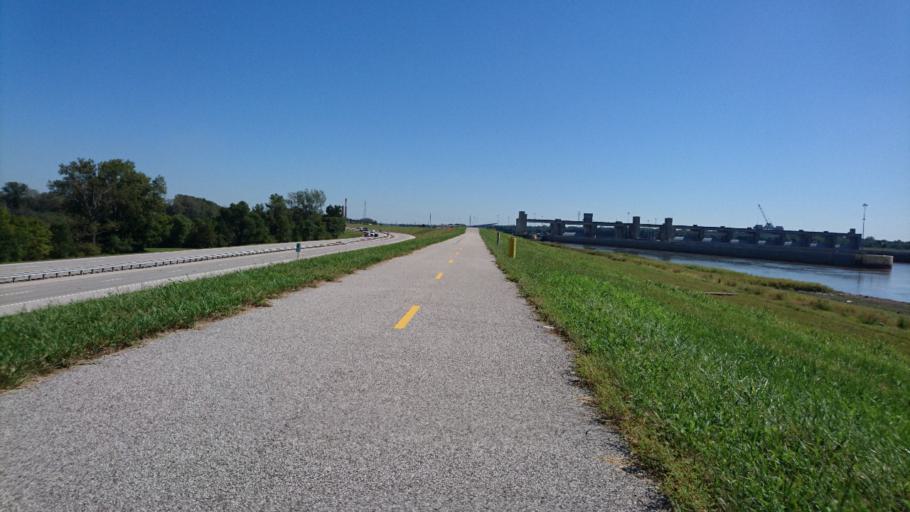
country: US
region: Illinois
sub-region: Madison County
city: Alton
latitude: 38.8753
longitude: -90.1565
